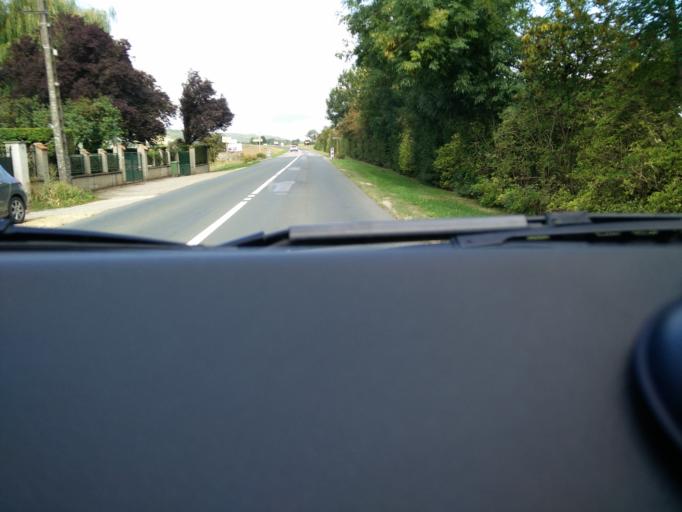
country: FR
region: Lorraine
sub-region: Departement de la Meuse
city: Etain
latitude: 49.1116
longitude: 5.5916
